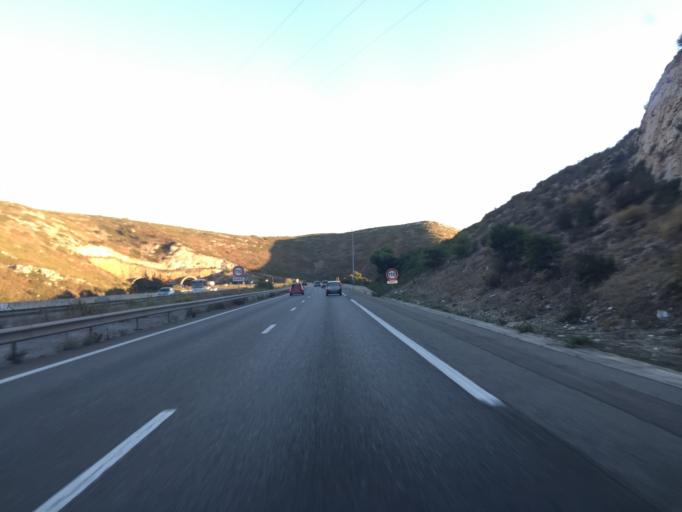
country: FR
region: Provence-Alpes-Cote d'Azur
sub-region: Departement des Bouches-du-Rhone
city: Marseille 16
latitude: 43.3736
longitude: 5.3197
